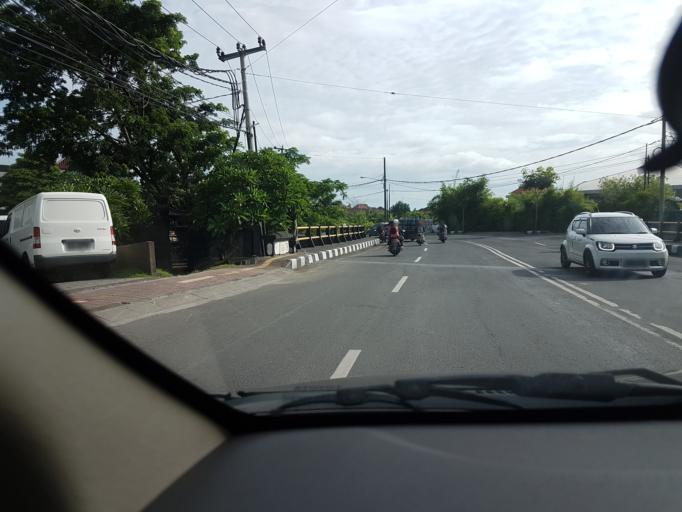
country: ID
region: Bali
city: Denpasar
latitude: -8.6723
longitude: 115.1909
